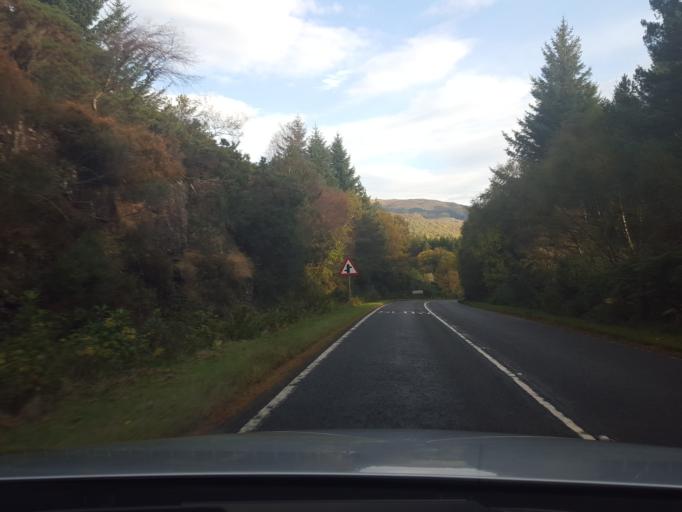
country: GB
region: Scotland
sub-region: Highland
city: Portree
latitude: 57.2869
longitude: -5.6547
